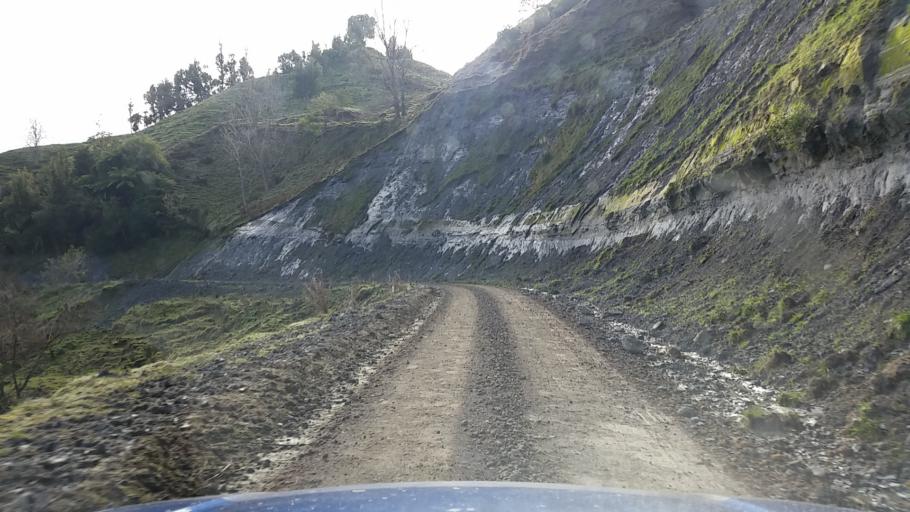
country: NZ
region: Taranaki
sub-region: New Plymouth District
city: Waitara
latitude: -39.1089
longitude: 174.8484
